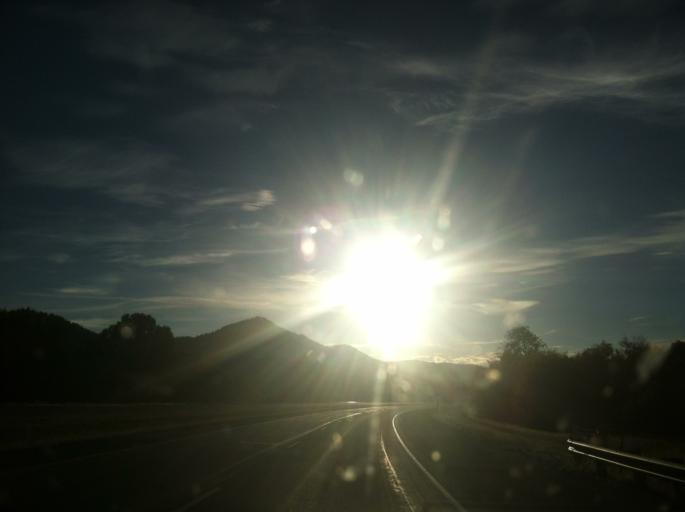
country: US
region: Montana
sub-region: Missoula County
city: Clinton
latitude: 46.6958
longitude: -113.4137
